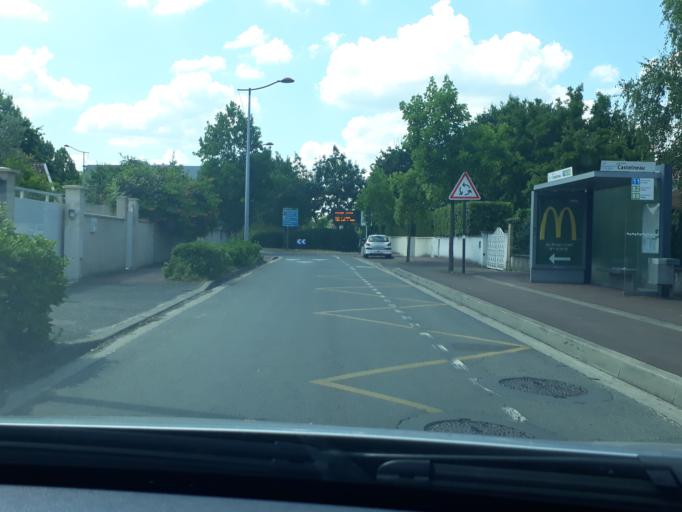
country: FR
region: Aquitaine
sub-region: Departement de la Gironde
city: Le Haillan
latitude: 44.8426
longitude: -0.6692
